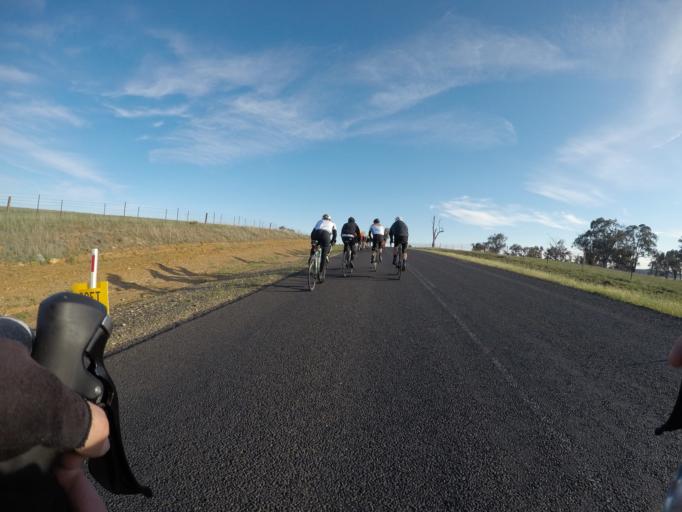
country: AU
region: New South Wales
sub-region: Cabonne
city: Molong
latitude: -32.9916
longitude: 148.7877
